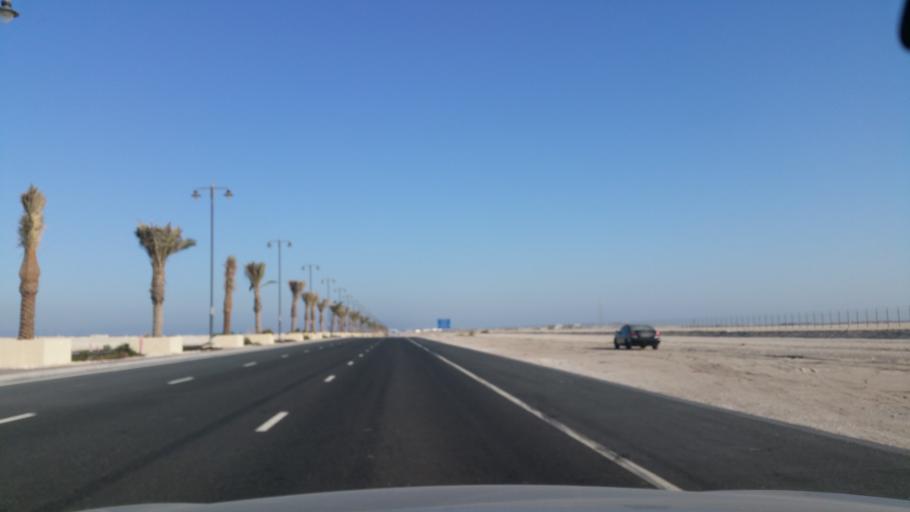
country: QA
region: Al Wakrah
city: Umm Sa'id
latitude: 25.0604
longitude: 51.5874
